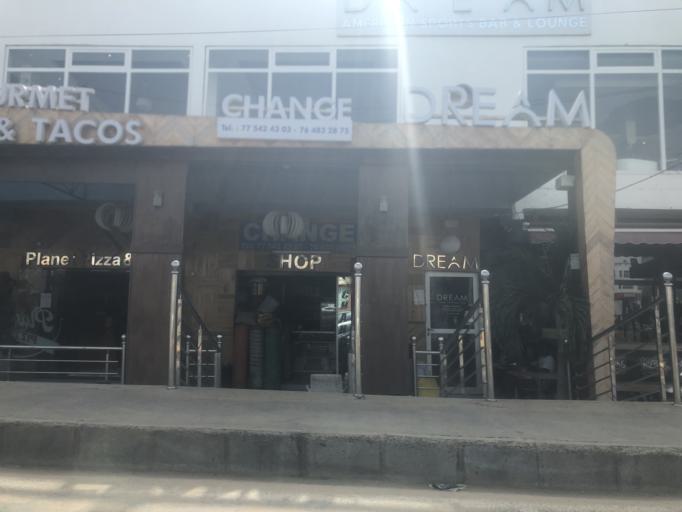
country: SN
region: Dakar
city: Mermoz Boabab
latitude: 14.7434
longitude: -17.5119
